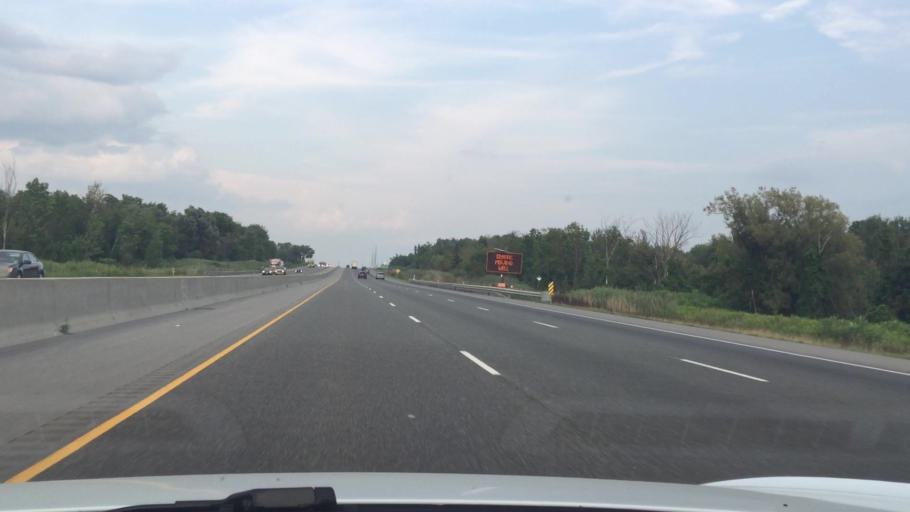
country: CA
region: Ontario
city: Cobourg
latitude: 43.9408
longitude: -78.4454
